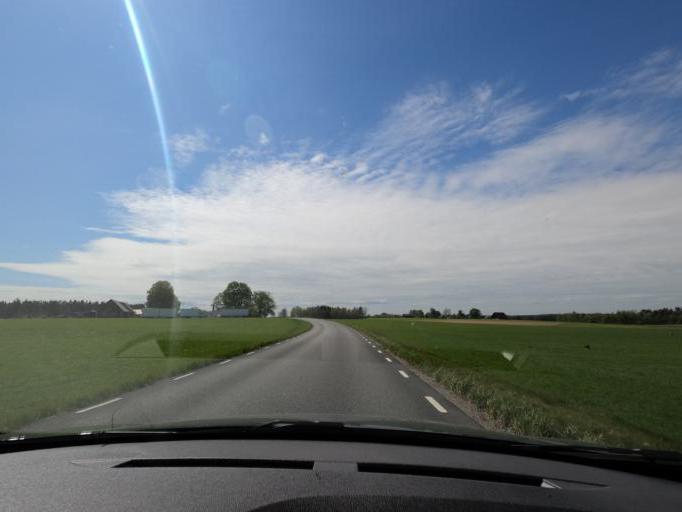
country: SE
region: Joenkoeping
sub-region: Varnamo Kommun
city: Bredaryd
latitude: 57.1421
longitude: 13.7145
